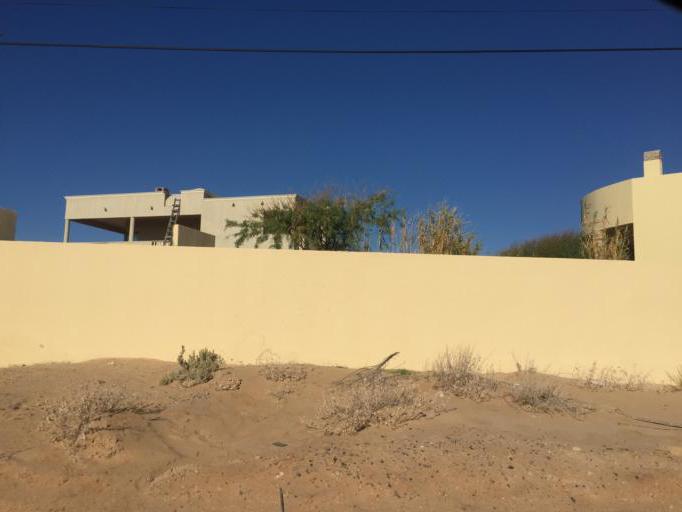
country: MX
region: Sonora
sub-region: Puerto Penasco
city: Puerto Penasco
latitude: 31.2877
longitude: -113.4771
